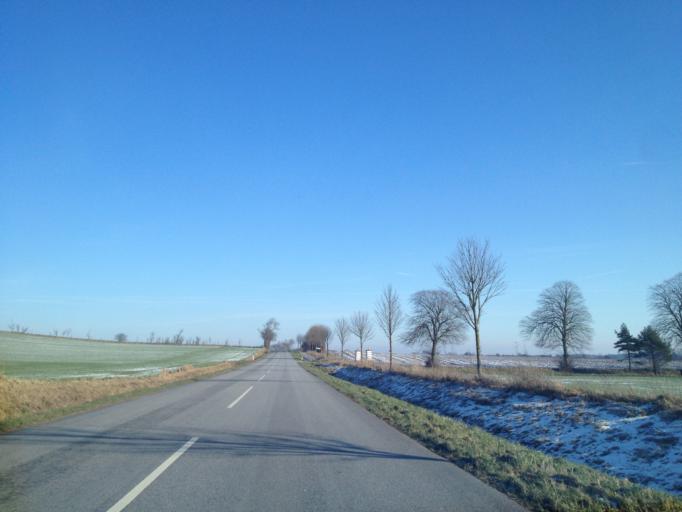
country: DK
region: South Denmark
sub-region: Haderslev Kommune
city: Starup
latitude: 55.2748
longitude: 9.5690
